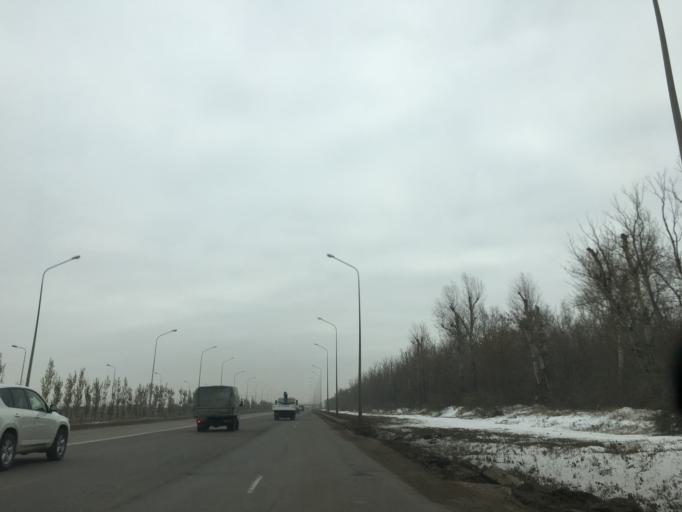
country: KZ
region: Astana Qalasy
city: Astana
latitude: 51.1654
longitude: 71.5053
